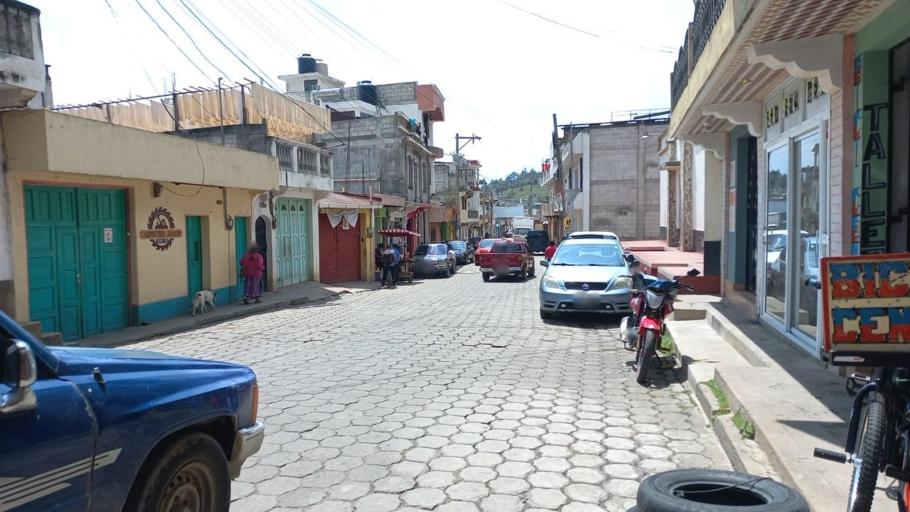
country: GT
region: Totonicapan
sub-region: Municipio de San Andres Xecul
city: San Andres Xecul
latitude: 14.9037
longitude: -91.4822
